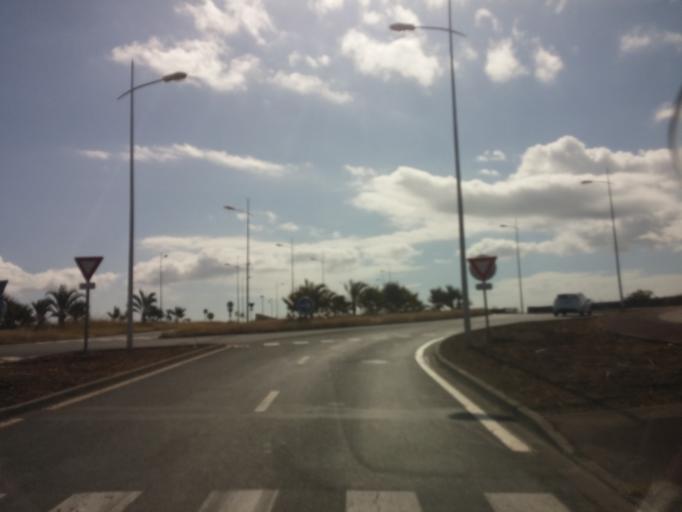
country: RE
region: Reunion
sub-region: Reunion
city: Le Port
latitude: -20.9602
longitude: 55.2938
